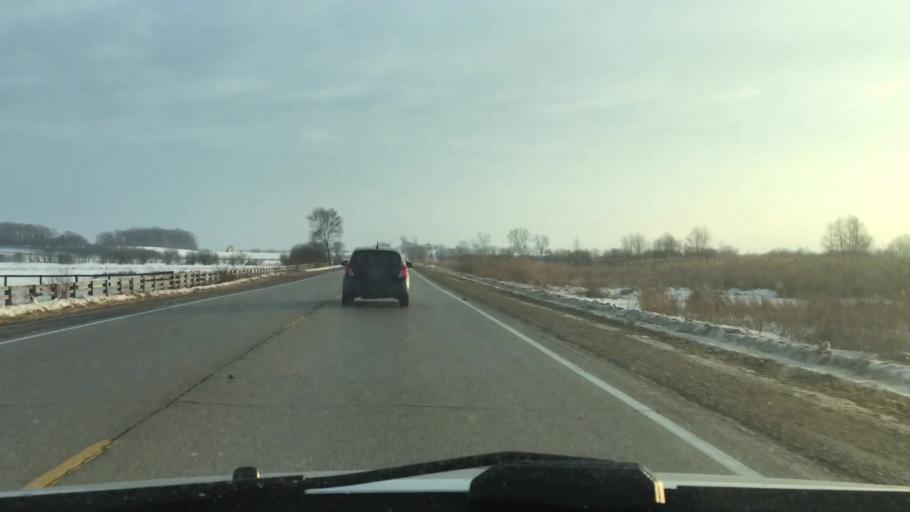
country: US
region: Illinois
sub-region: McHenry County
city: Huntley
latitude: 42.2217
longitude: -88.4229
